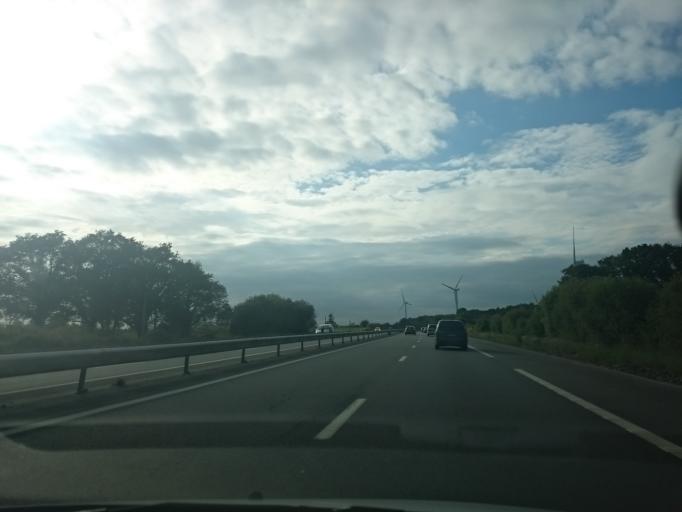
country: FR
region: Pays de la Loire
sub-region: Departement de la Loire-Atlantique
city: Prinquiau
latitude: 47.4056
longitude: -2.0116
